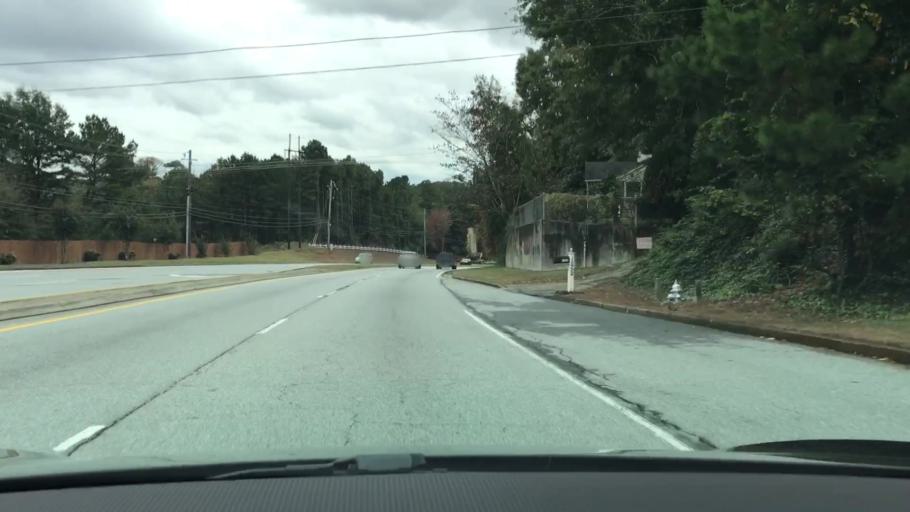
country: US
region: Georgia
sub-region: Gwinnett County
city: Lawrenceville
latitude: 33.9830
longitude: -84.0216
